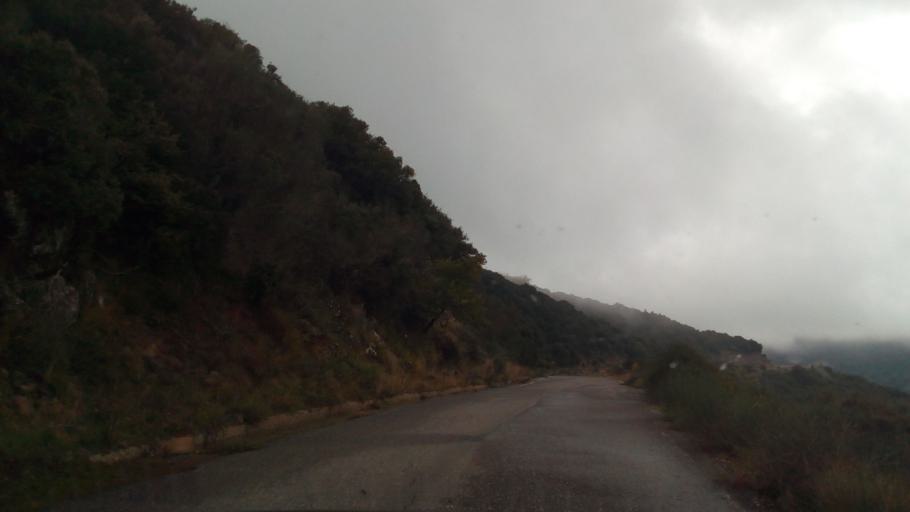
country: GR
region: West Greece
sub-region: Nomos Aitolias kai Akarnanias
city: Nafpaktos
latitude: 38.5127
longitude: 21.8360
